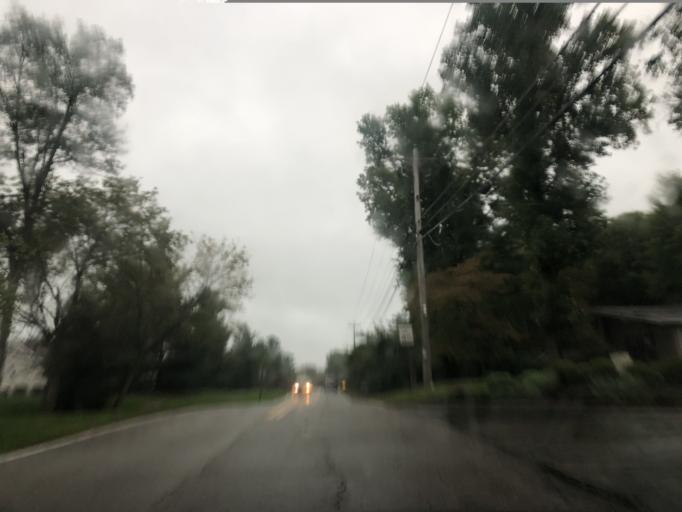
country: US
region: Ohio
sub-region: Clermont County
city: Mulberry
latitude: 39.1962
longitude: -84.2484
